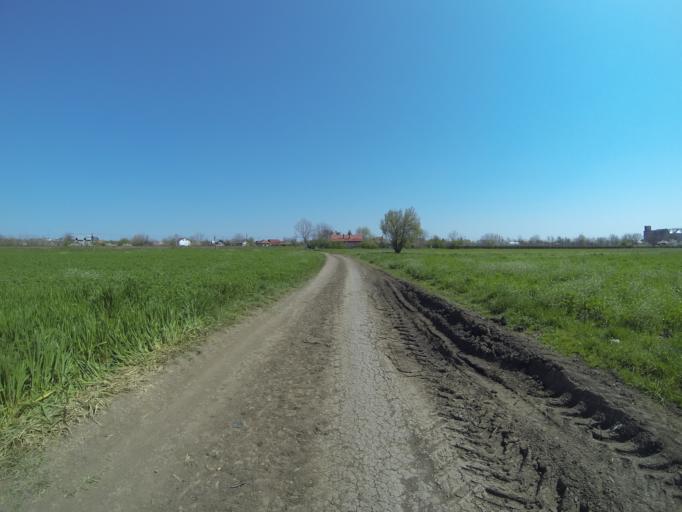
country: RO
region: Dolj
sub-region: Comuna Segarcea
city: Segarcea
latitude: 44.0911
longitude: 23.7272
